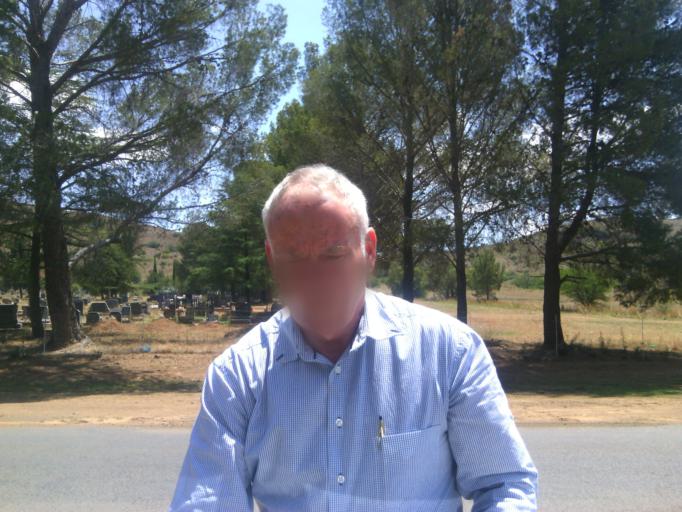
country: ZA
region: Orange Free State
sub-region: Xhariep District Municipality
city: Dewetsdorp
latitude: -29.5768
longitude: 26.6638
